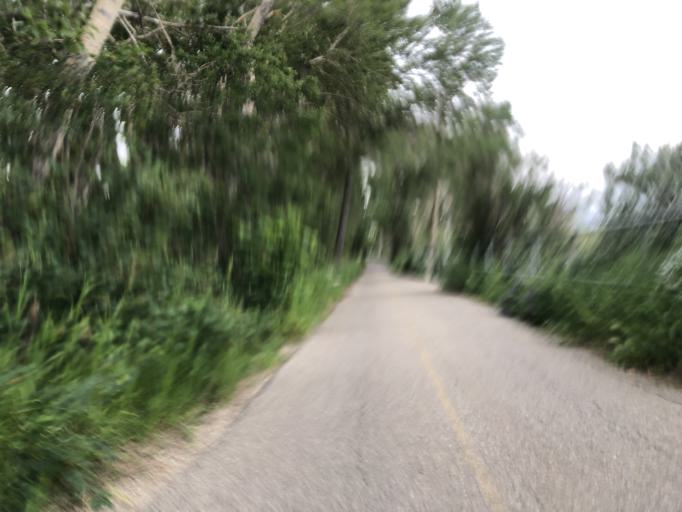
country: CA
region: Alberta
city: Calgary
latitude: 51.0426
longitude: -114.0230
